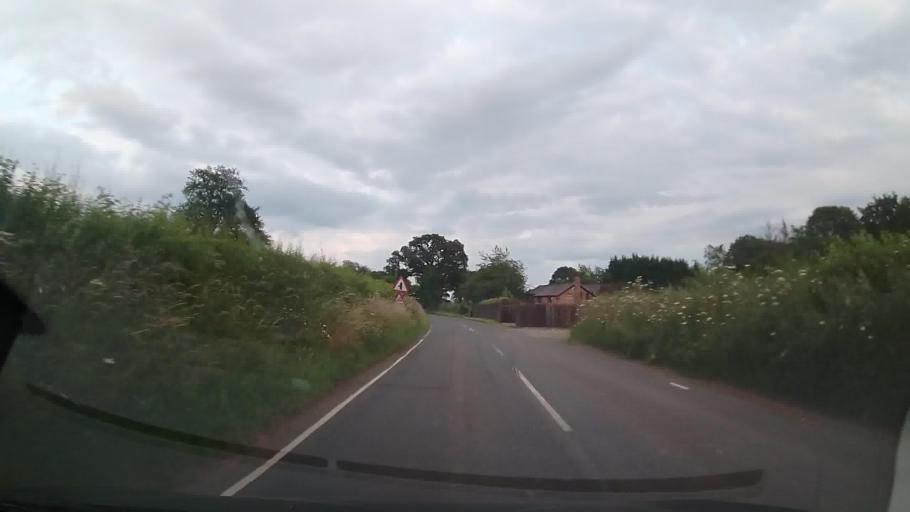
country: GB
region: England
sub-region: Shropshire
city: Great Ness
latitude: 52.7981
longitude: -2.9316
